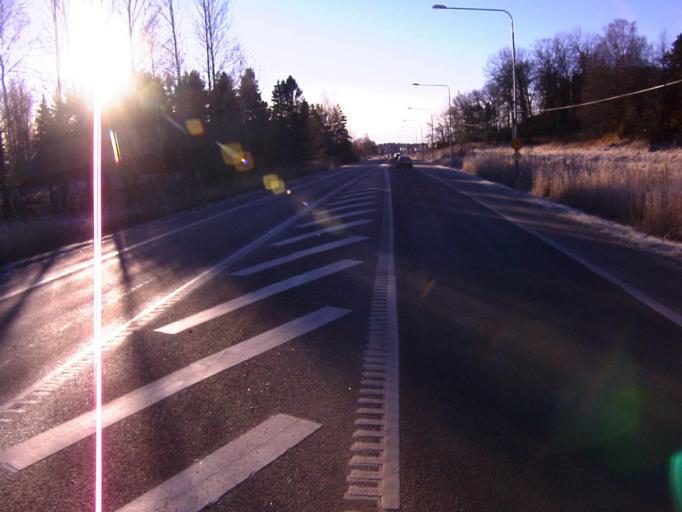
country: SE
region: Soedermanland
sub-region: Eskilstuna Kommun
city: Torshalla
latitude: 59.4001
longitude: 16.4724
